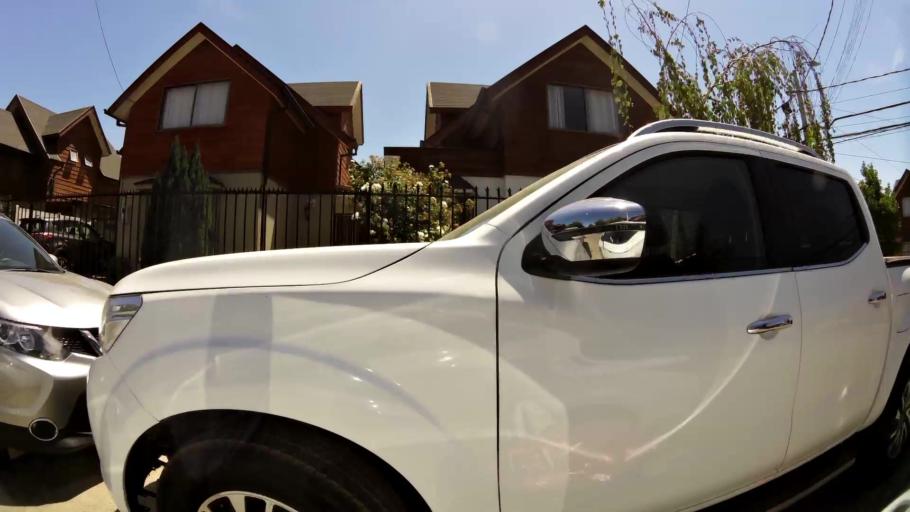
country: CL
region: Maule
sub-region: Provincia de Talca
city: Talca
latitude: -35.4260
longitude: -71.6140
